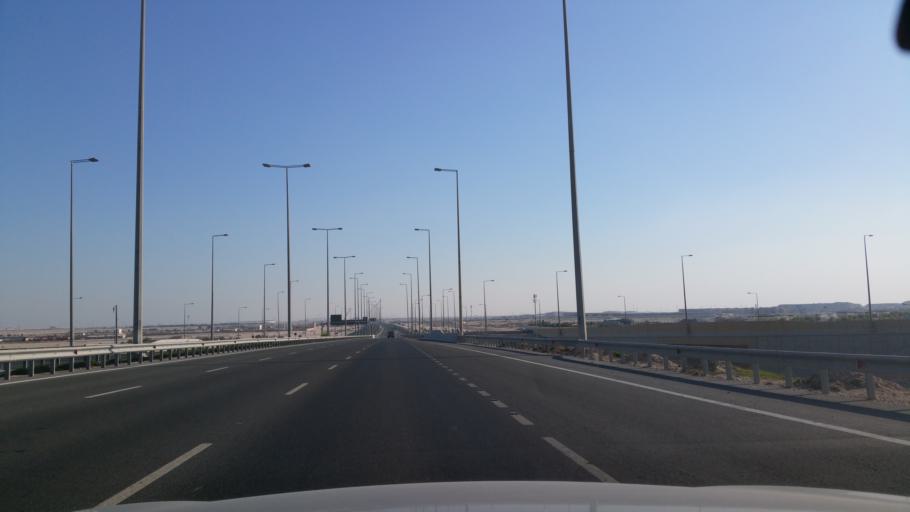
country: QA
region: Al Wakrah
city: Al Wukayr
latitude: 25.1644
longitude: 51.4723
